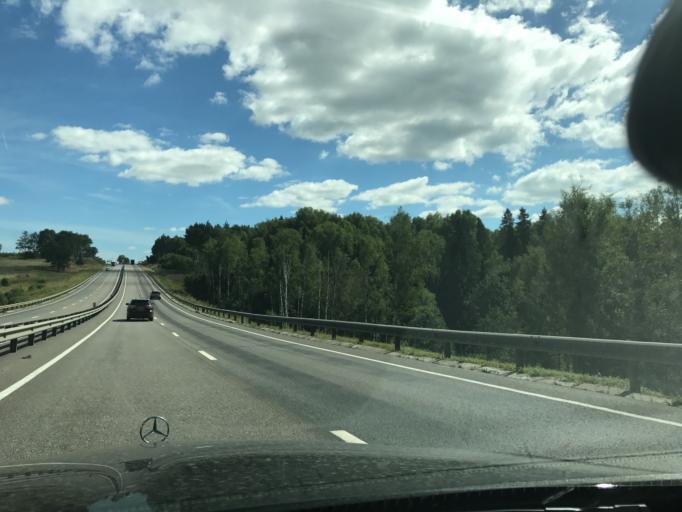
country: RU
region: Vladimir
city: Novovyazniki
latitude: 56.1712
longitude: 42.4292
